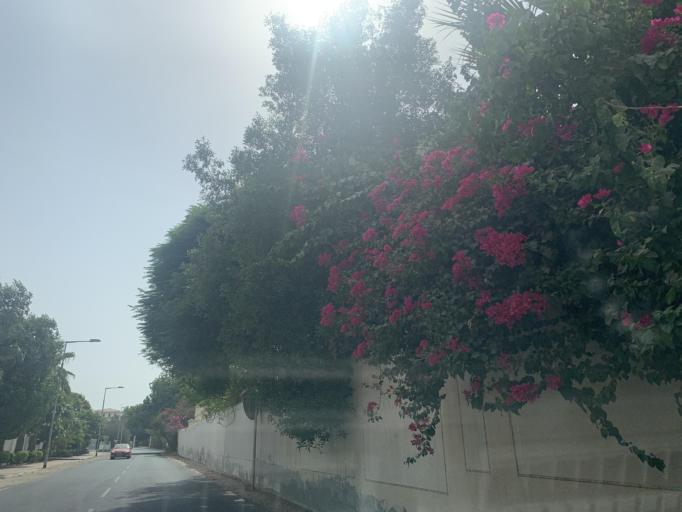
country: BH
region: Manama
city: Jidd Hafs
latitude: 26.2034
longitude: 50.4790
